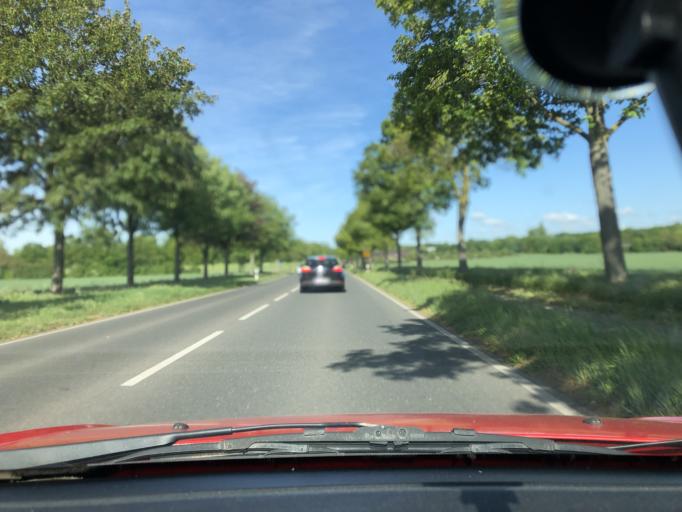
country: DE
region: North Rhine-Westphalia
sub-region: Regierungsbezirk Dusseldorf
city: Moers
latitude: 51.4917
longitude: 6.6207
